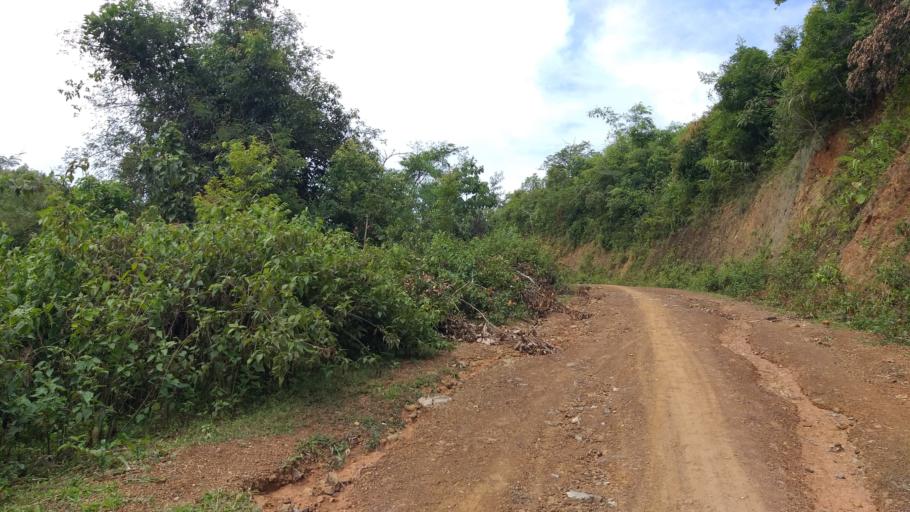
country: VN
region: Huyen Dien Bien
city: Dien Bien Phu
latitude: 21.4211
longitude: 102.6862
